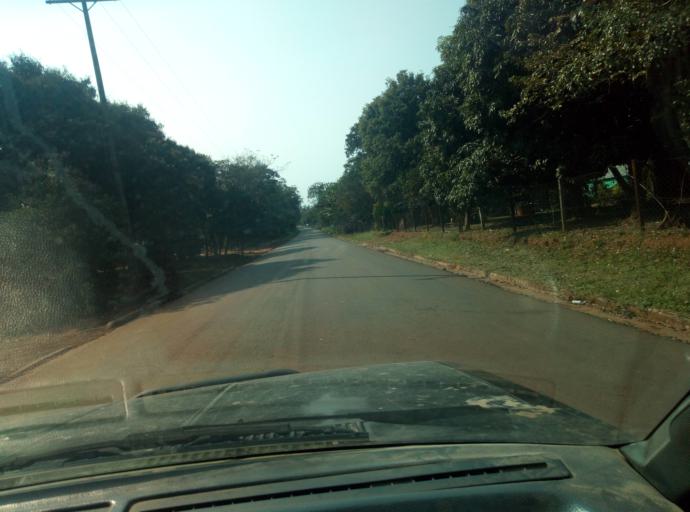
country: PY
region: Caaguazu
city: Carayao
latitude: -25.2103
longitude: -56.3024
